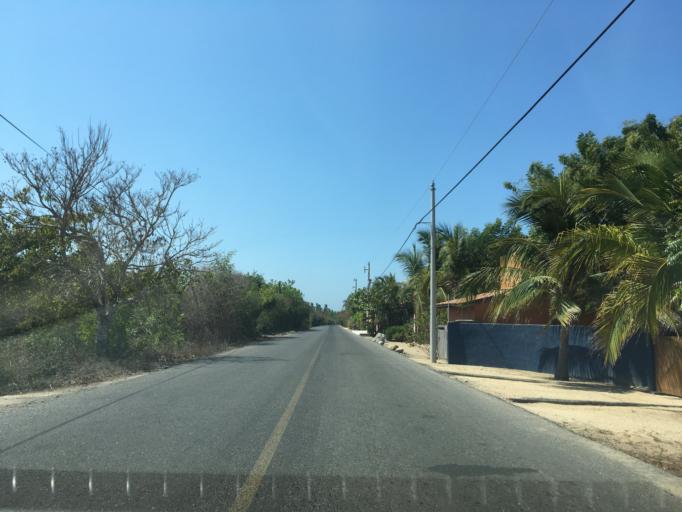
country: MX
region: Guerrero
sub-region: Zihuatanejo de Azueta
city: Los Achotes
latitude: 17.5511
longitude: -101.4384
